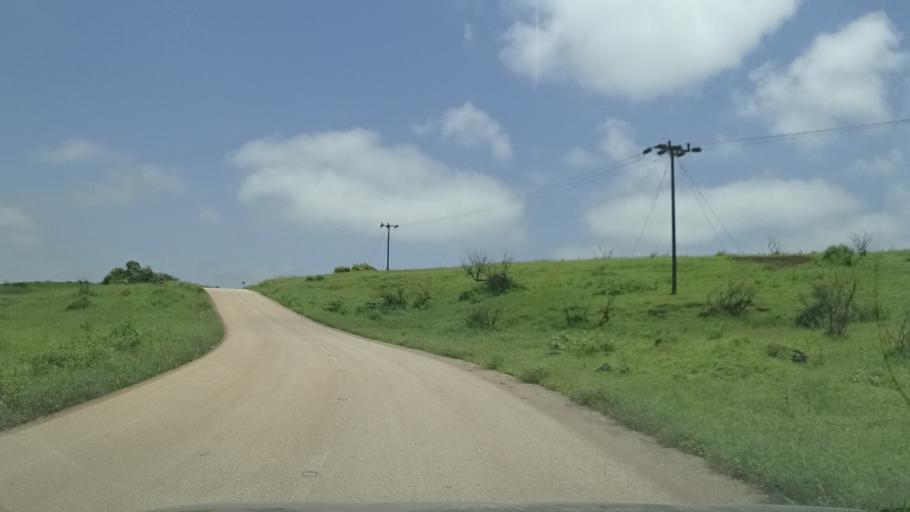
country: OM
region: Zufar
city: Salalah
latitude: 17.2143
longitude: 54.1996
